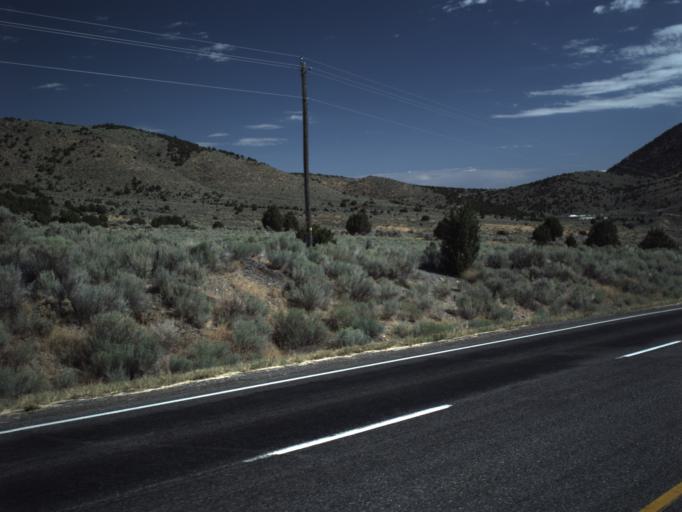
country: US
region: Utah
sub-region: Utah County
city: Genola
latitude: 39.9671
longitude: -112.0913
